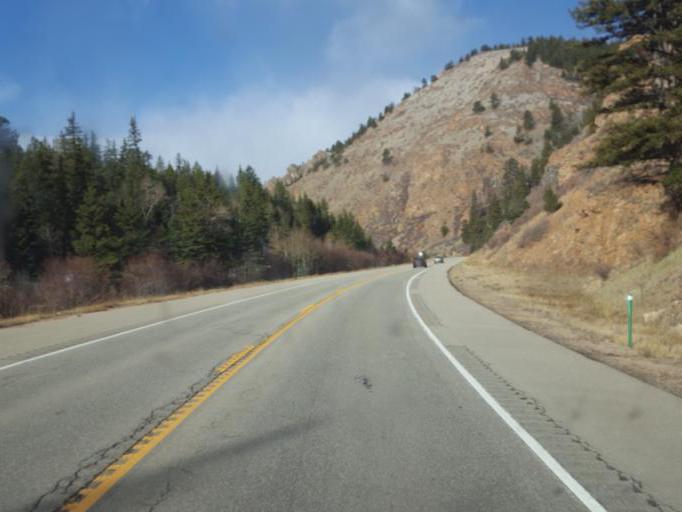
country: US
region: Colorado
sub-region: Clear Creek County
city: Georgetown
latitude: 39.4614
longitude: -105.6786
